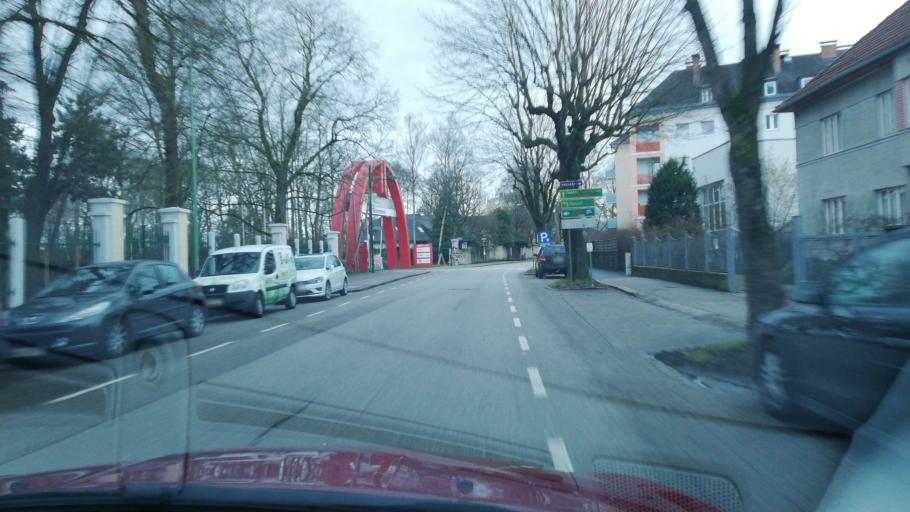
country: AT
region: Upper Austria
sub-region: Wels-Land
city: Thalheim bei Wels
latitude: 48.1546
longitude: 14.0158
